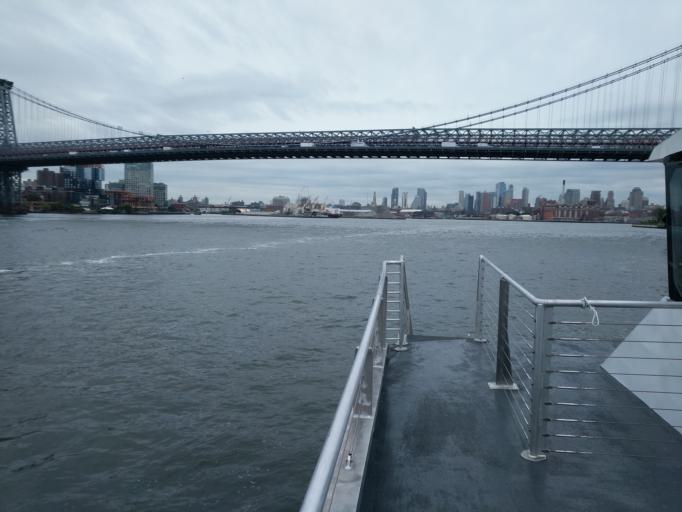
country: US
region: New York
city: New York City
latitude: 40.7165
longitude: -73.9724
